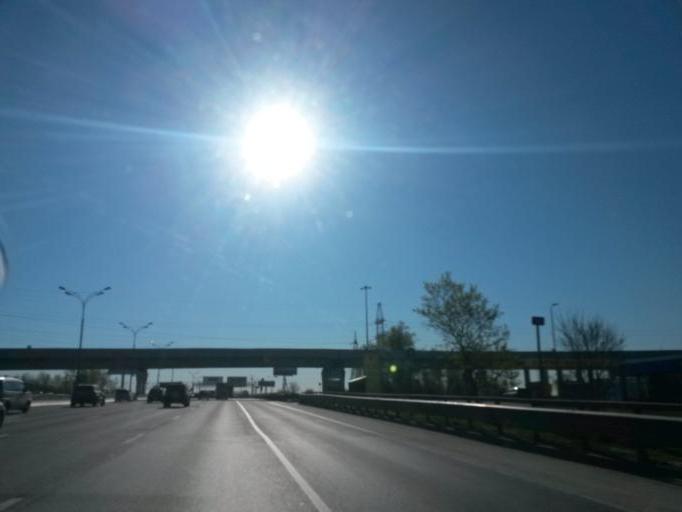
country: RU
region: Moskovskaya
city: Biryulevo Zapadnoye
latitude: 55.5733
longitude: 37.6404
